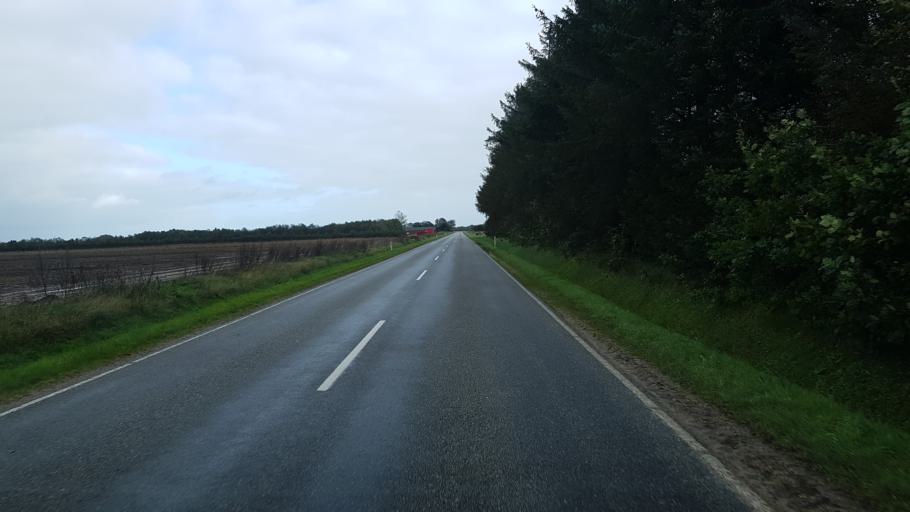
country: DK
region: South Denmark
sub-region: Varde Kommune
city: Olgod
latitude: 55.7603
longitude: 8.7654
